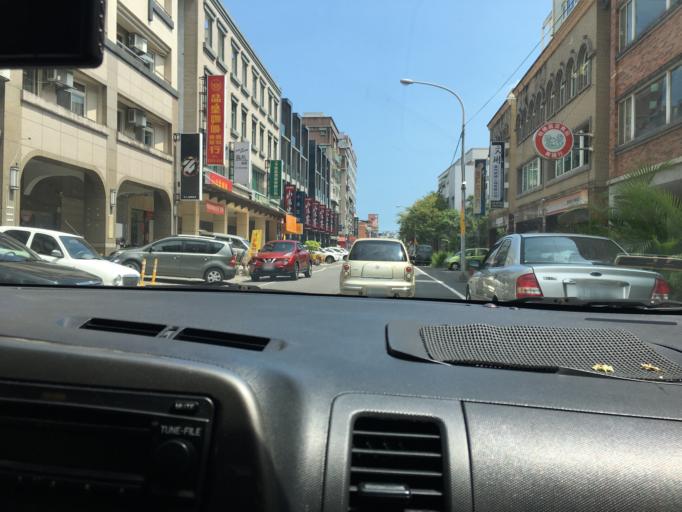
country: TW
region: Taiwan
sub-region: Yilan
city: Yilan
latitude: 24.7465
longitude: 121.7392
